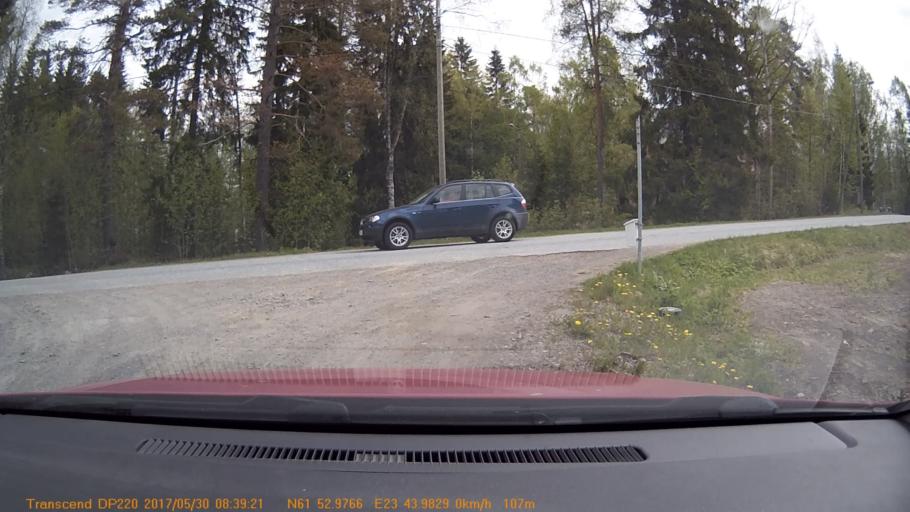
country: FI
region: Pirkanmaa
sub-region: Tampere
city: Kuru
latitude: 61.8829
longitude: 23.7330
